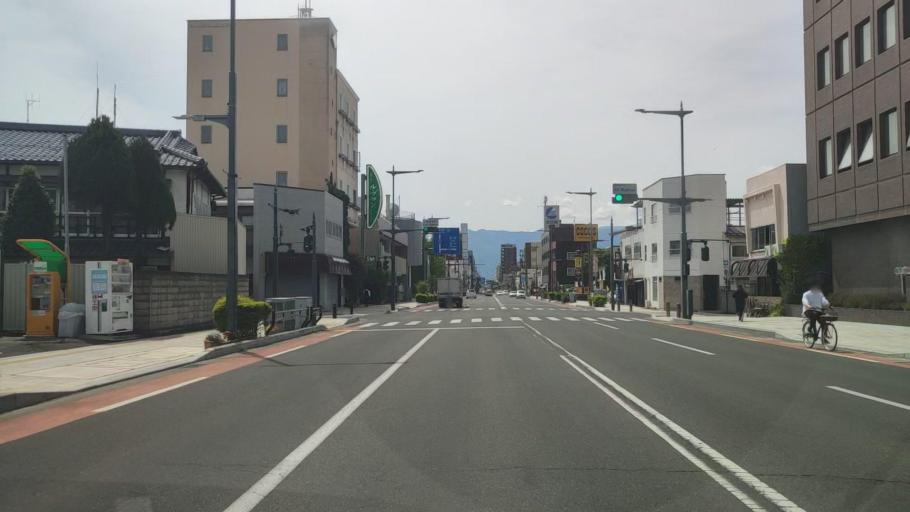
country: JP
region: Nagano
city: Matsumoto
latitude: 36.2312
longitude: 137.9760
